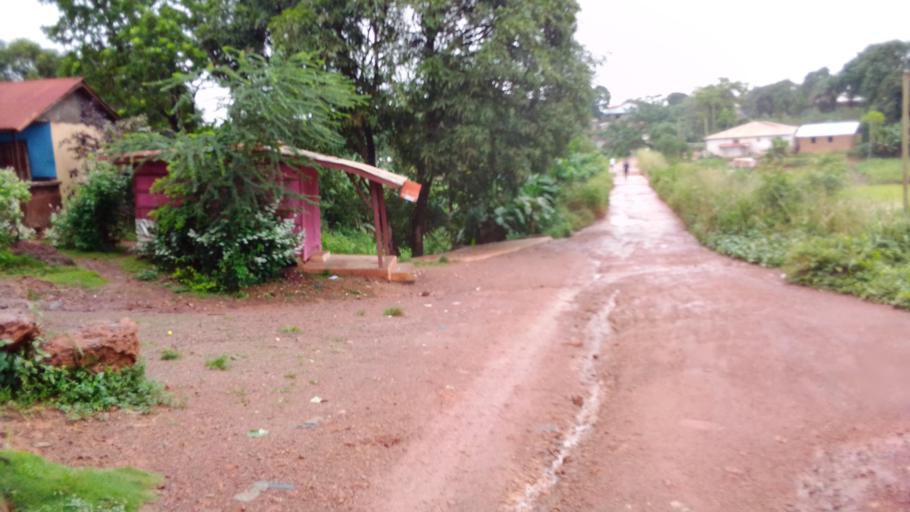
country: SL
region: Eastern Province
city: Kenema
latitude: 7.8880
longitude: -11.1777
